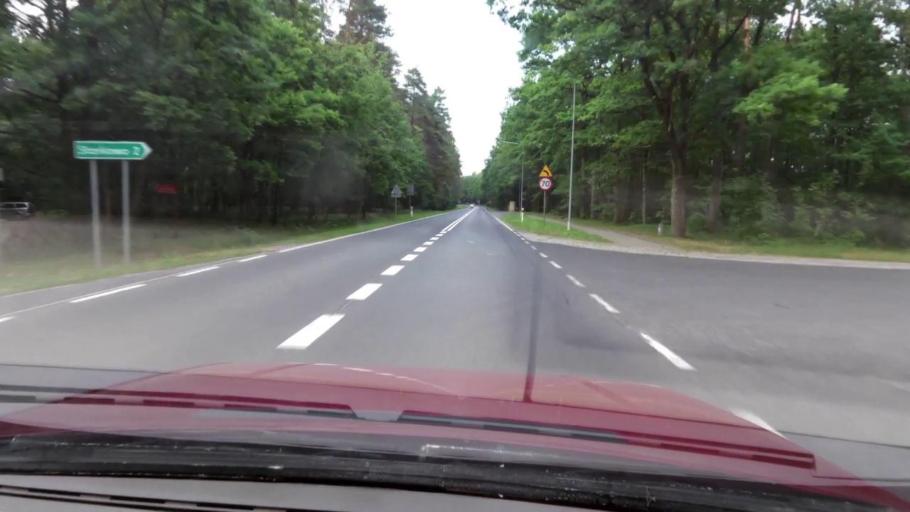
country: PL
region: Pomeranian Voivodeship
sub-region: Powiat bytowski
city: Trzebielino
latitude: 54.2518
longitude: 17.1029
